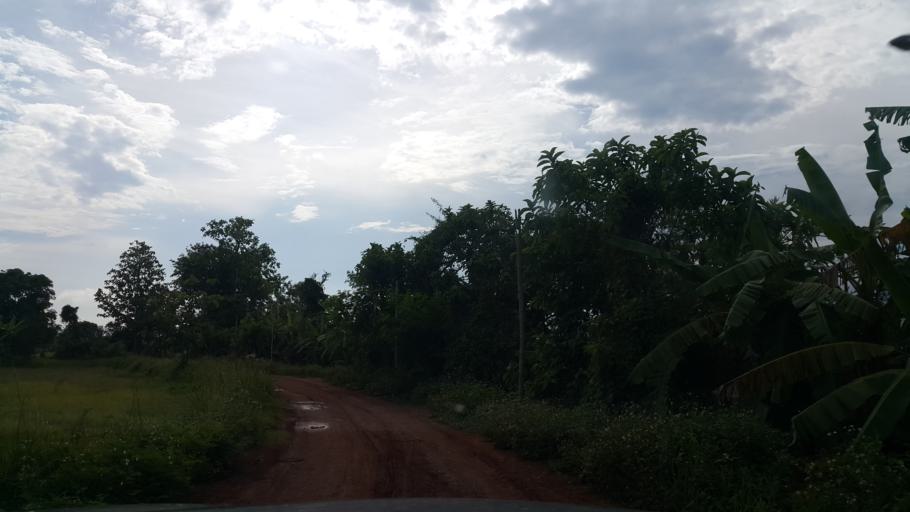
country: TH
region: Chiang Rai
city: Wiang Chai
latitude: 19.9751
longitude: 99.9120
